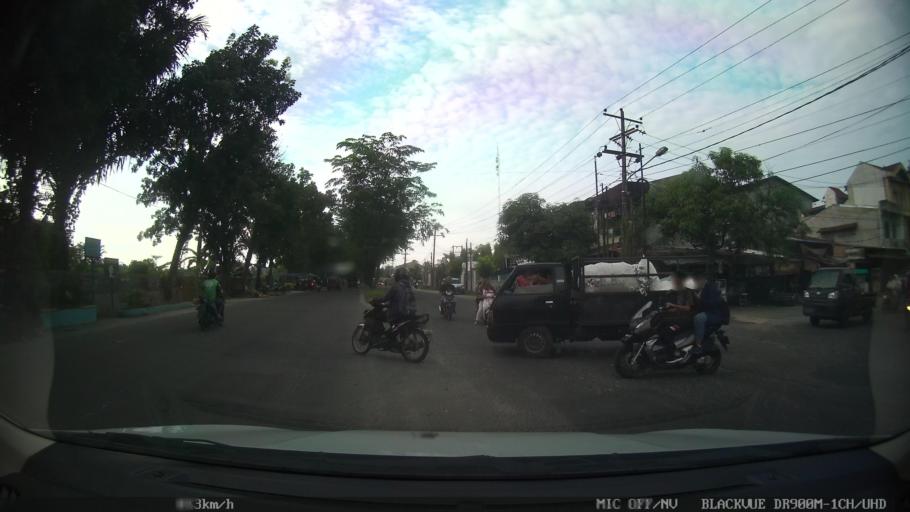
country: ID
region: North Sumatra
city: Sunggal
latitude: 3.5629
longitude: 98.6161
